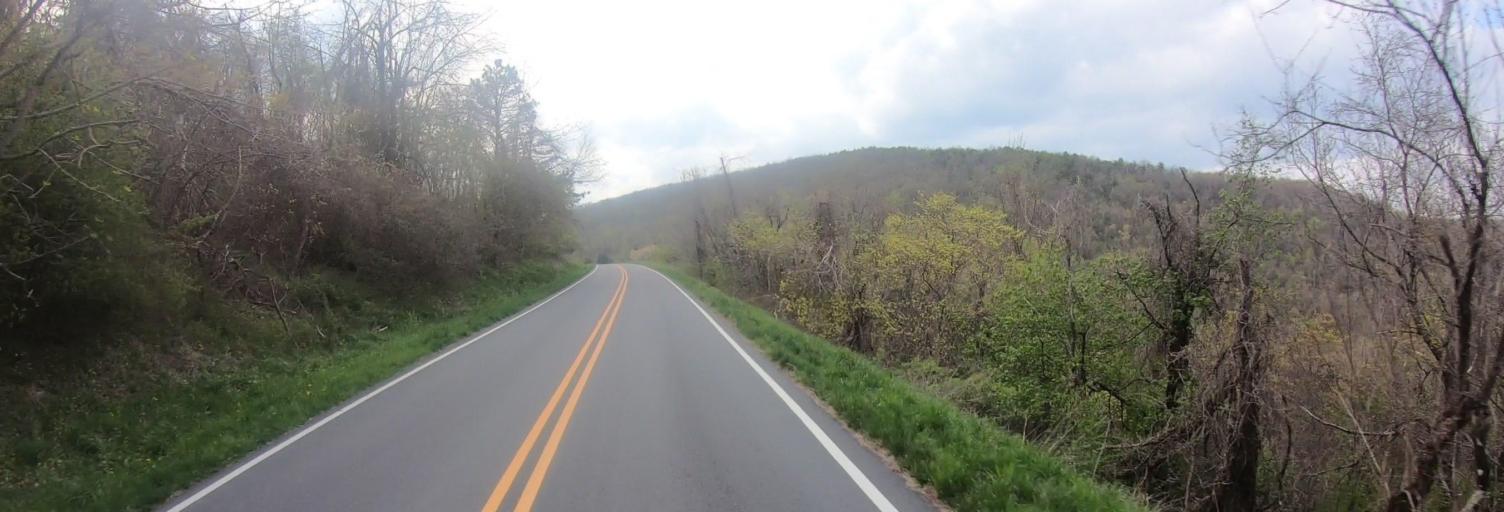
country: US
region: Virginia
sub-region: Augusta County
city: Dooms
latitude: 38.0713
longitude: -78.7911
